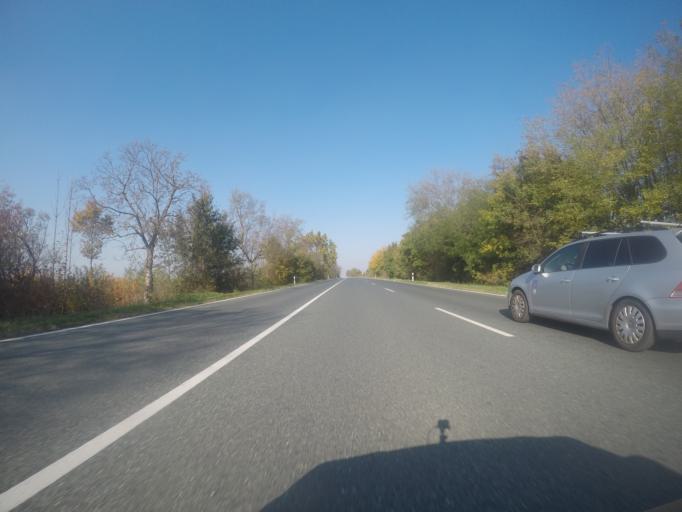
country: HU
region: Tolna
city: Madocsa
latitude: 46.6986
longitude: 18.8874
